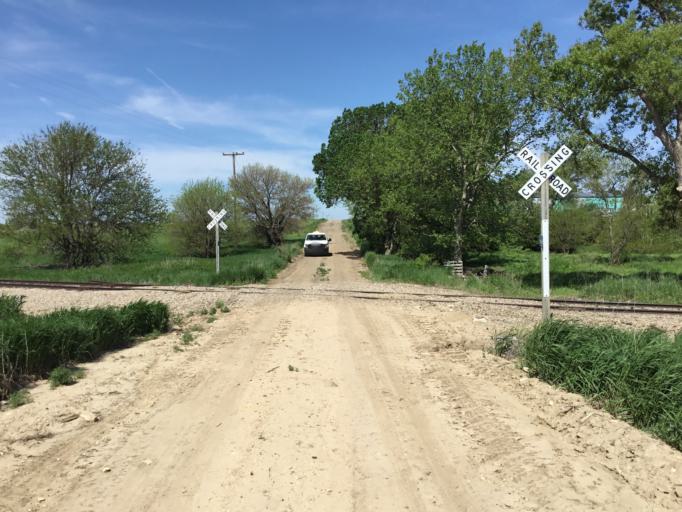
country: US
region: Kansas
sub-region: Mitchell County
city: Beloit
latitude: 39.4955
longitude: -98.0346
